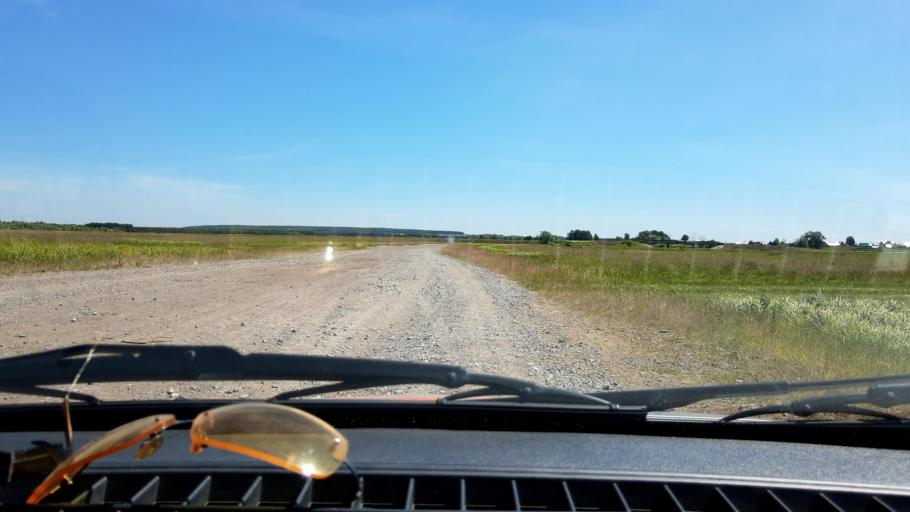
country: RU
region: Bashkortostan
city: Mikhaylovka
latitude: 54.9688
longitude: 55.7967
